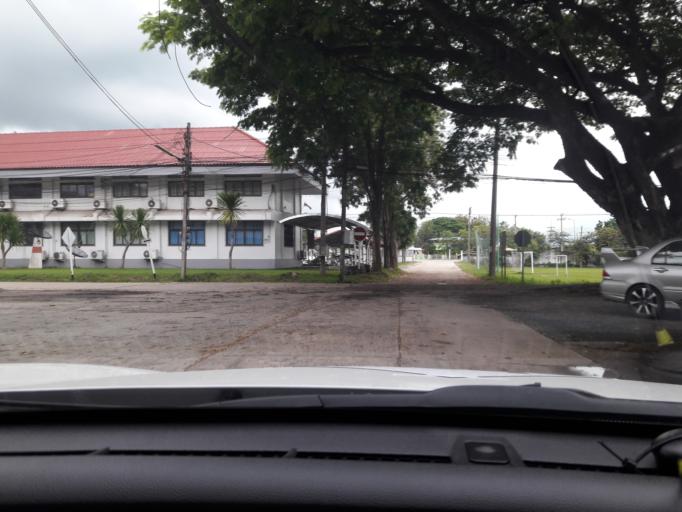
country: TH
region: Nakhon Sawan
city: Tak Fa
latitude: 15.3490
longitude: 100.4954
